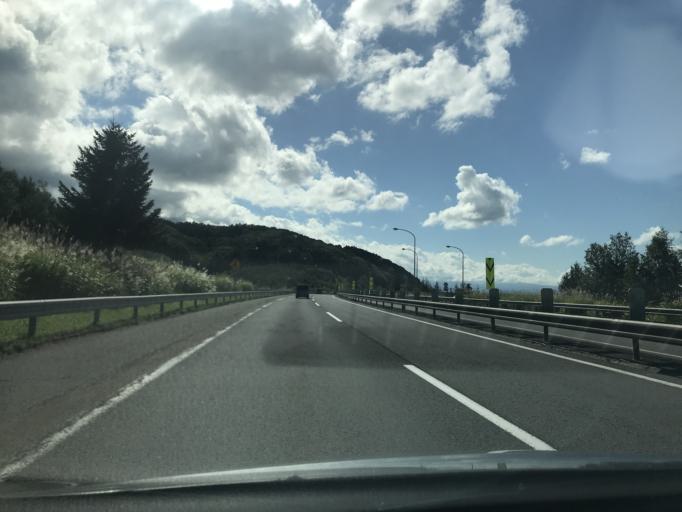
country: JP
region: Hokkaido
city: Fukagawa
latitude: 43.7086
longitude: 142.1441
